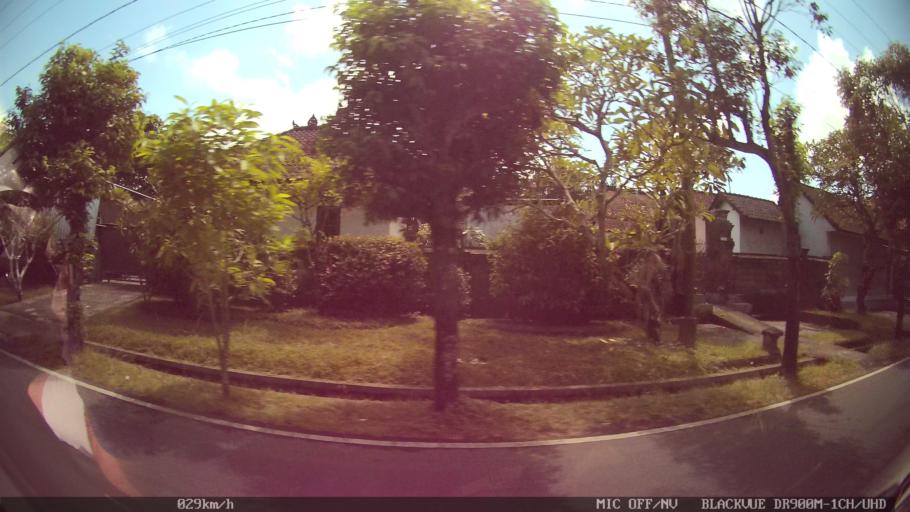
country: ID
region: Bali
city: Banjar Jabejero
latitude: -8.5925
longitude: 115.2585
